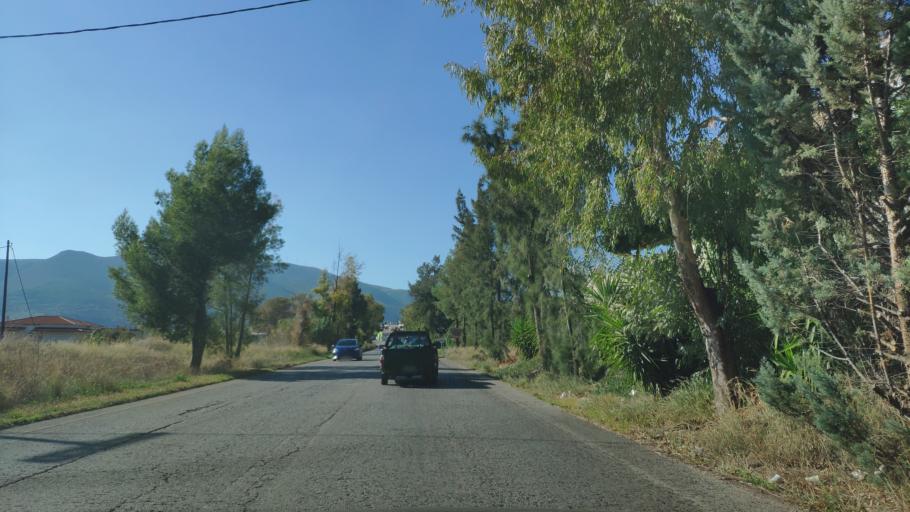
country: GR
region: Peloponnese
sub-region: Nomos Korinthias
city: Khiliomodhi
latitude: 37.8172
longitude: 22.8738
